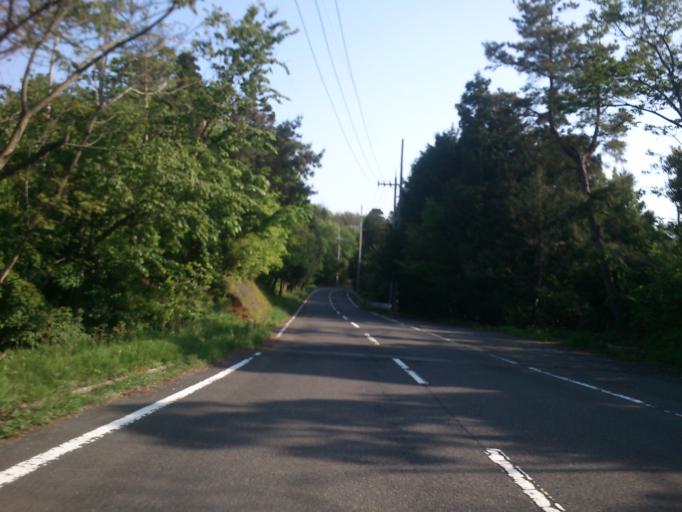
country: JP
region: Kyoto
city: Miyazu
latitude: 35.7437
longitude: 135.1736
